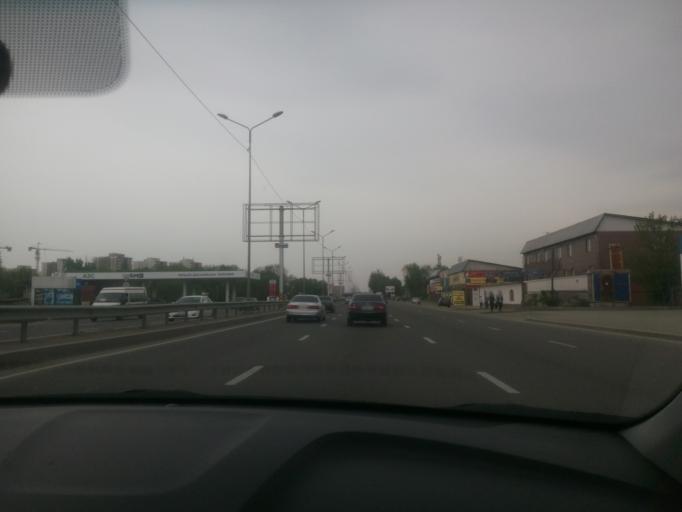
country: KZ
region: Almaty Qalasy
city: Almaty
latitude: 43.2371
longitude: 76.8069
